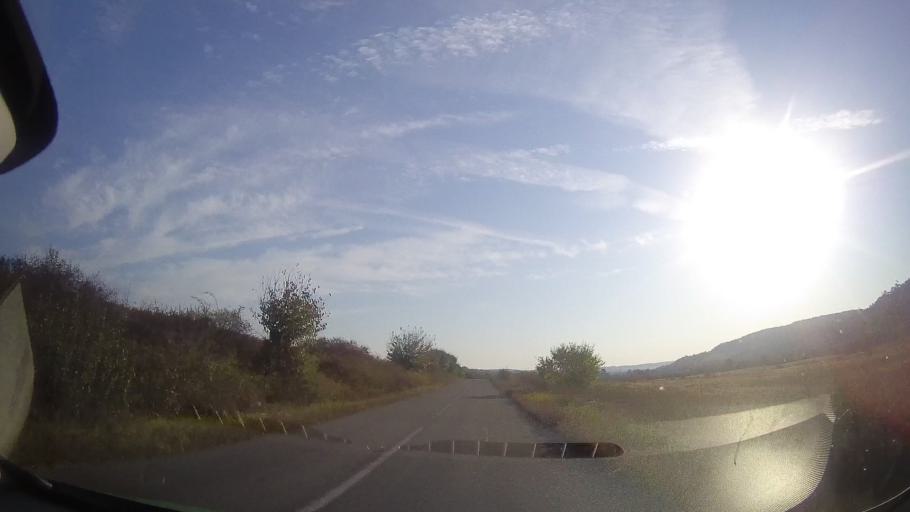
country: RO
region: Timis
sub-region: Comuna Bogda
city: Bogda
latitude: 45.9813
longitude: 21.5346
